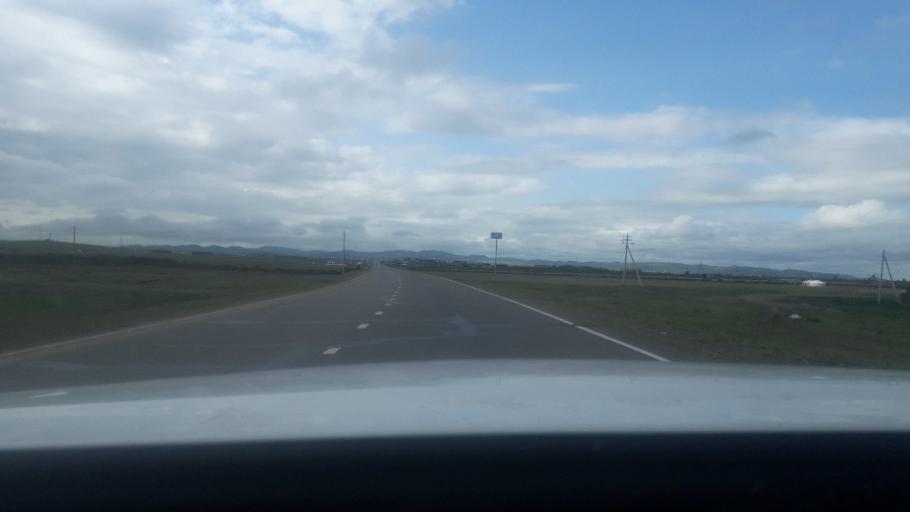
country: MN
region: Central Aimak
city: Altanbulag
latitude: 47.8080
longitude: 106.6381
